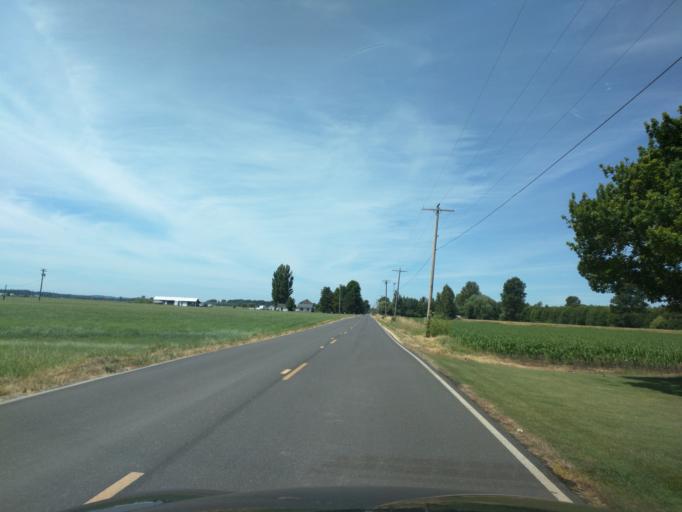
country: US
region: Washington
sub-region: Whatcom County
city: Lynden
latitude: 48.9349
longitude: -122.4225
